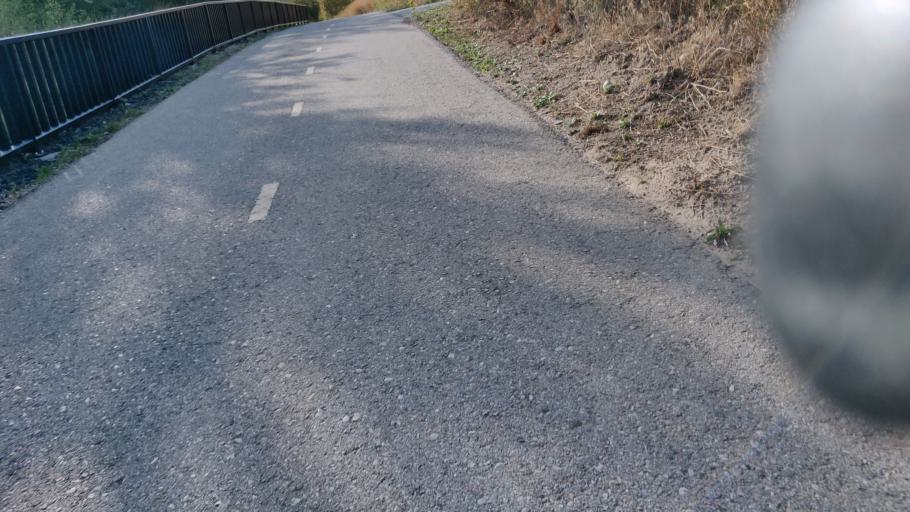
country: US
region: Idaho
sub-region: Ada County
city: Boise
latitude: 43.5783
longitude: -116.1479
